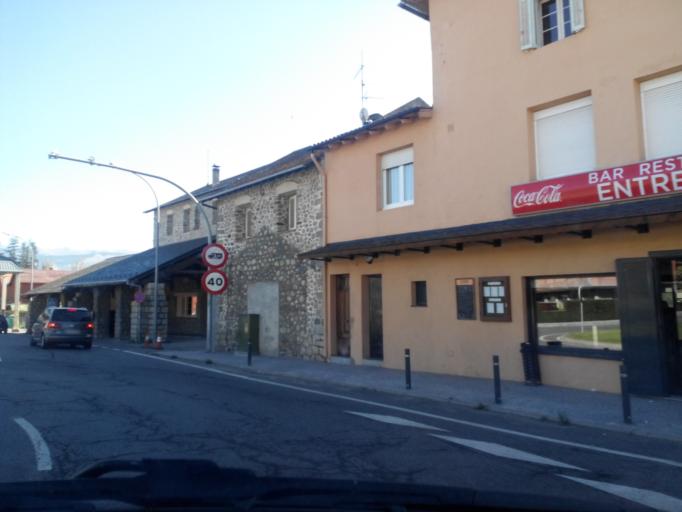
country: FR
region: Languedoc-Roussillon
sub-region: Departement des Pyrenees-Orientales
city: la Guingueta d'Ix
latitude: 42.4331
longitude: 1.9365
